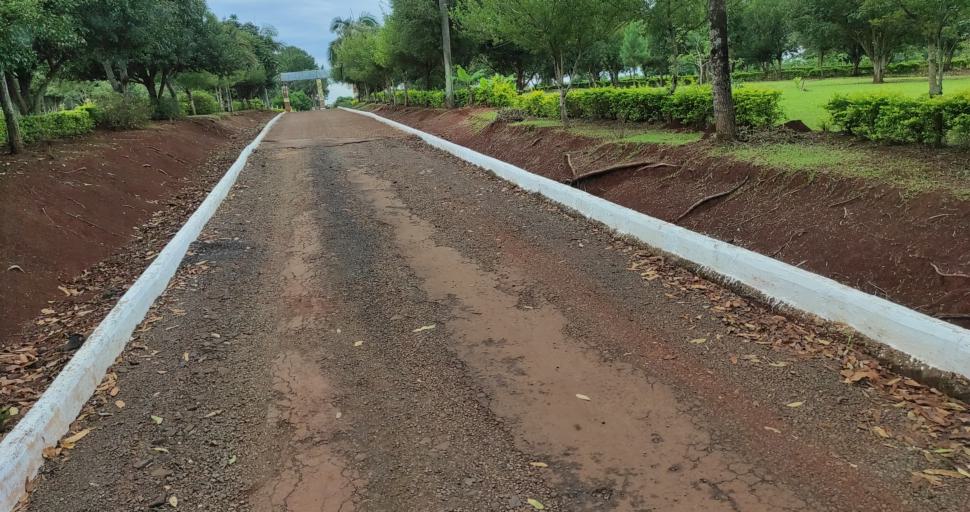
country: AR
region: Misiones
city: Puerto Libertad
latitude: -25.9581
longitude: -54.5967
